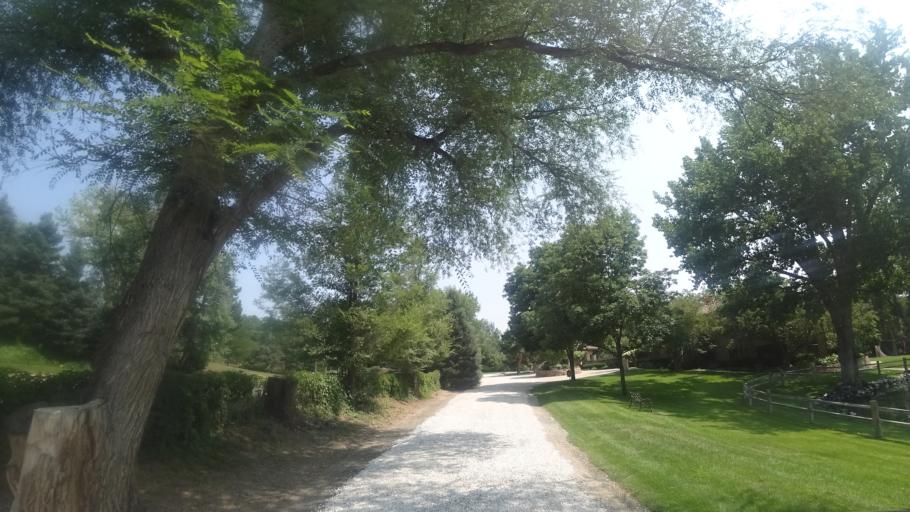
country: US
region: Colorado
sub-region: Arapahoe County
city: Cherry Hills Village
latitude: 39.6363
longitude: -104.9652
